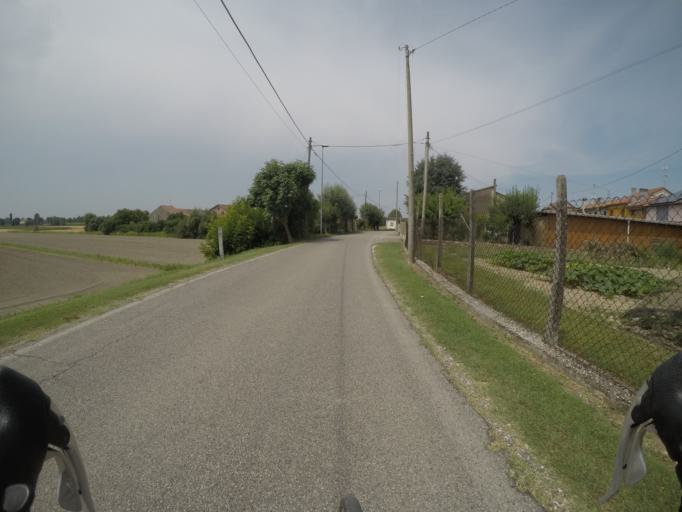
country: IT
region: Veneto
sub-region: Provincia di Rovigo
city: Villanova del Ghebbo Canton
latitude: 45.0504
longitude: 11.6504
